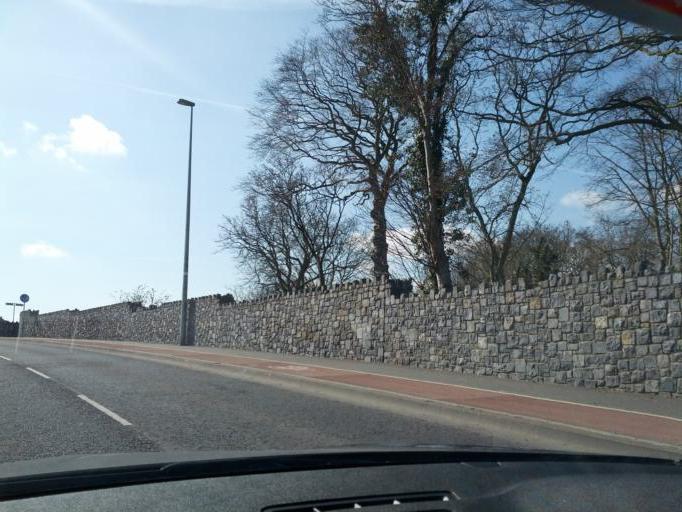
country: IE
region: Leinster
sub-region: Kildare
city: Maynooth
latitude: 53.3773
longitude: -6.5961
